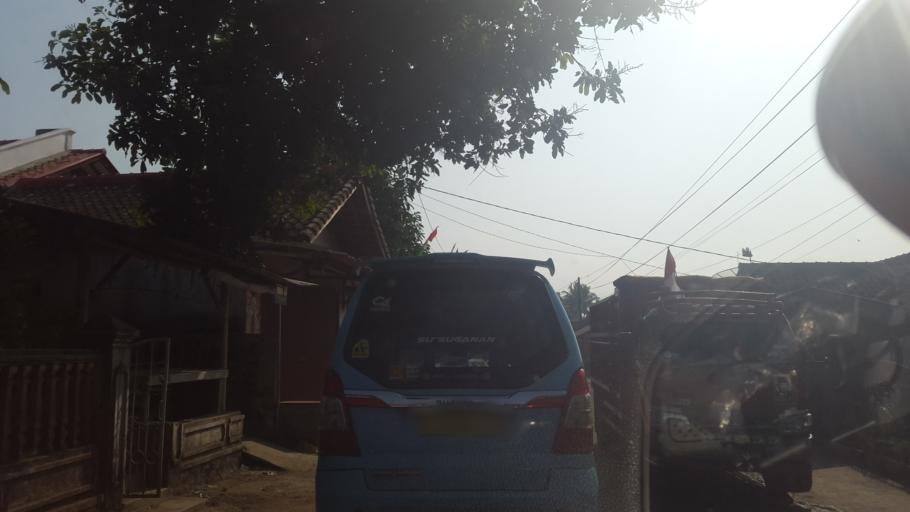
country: ID
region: West Java
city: Sukabumi
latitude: -6.8910
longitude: 106.8662
